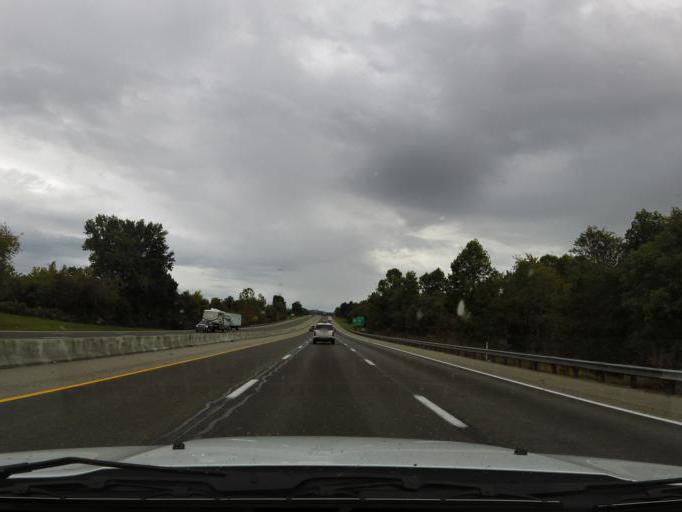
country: US
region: Kentucky
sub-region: Laurel County
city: London
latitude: 37.0738
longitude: -84.0990
